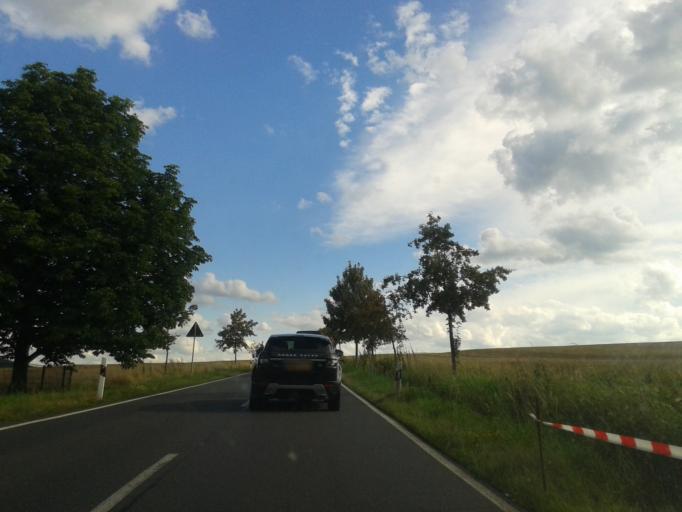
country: DE
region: Saxony
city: Durrrohrsdorf
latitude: 51.0345
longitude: 13.9533
